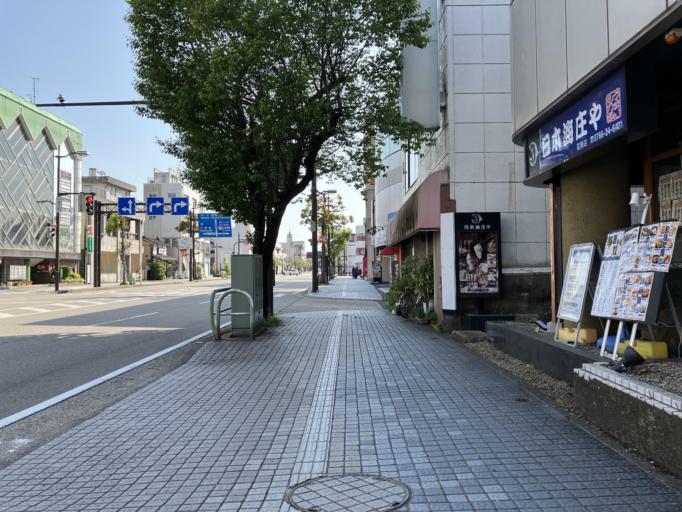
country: JP
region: Toyama
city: Takaoka
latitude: 36.7429
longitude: 137.0165
